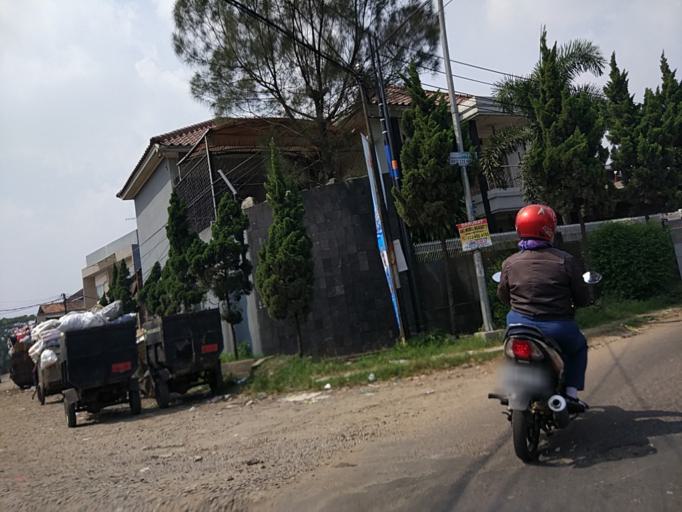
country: ID
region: West Java
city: Margahayukencana
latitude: -6.9323
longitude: 107.5738
